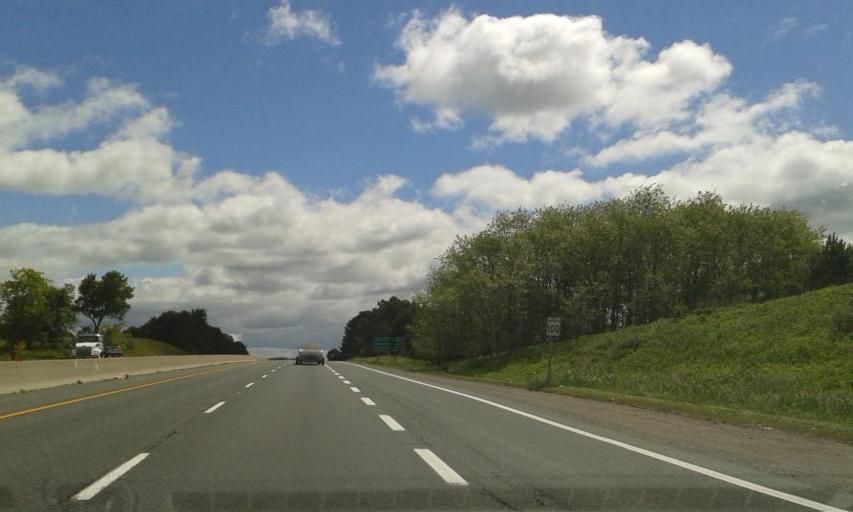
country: CA
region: Ontario
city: Quinte West
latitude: 44.0759
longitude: -77.7644
